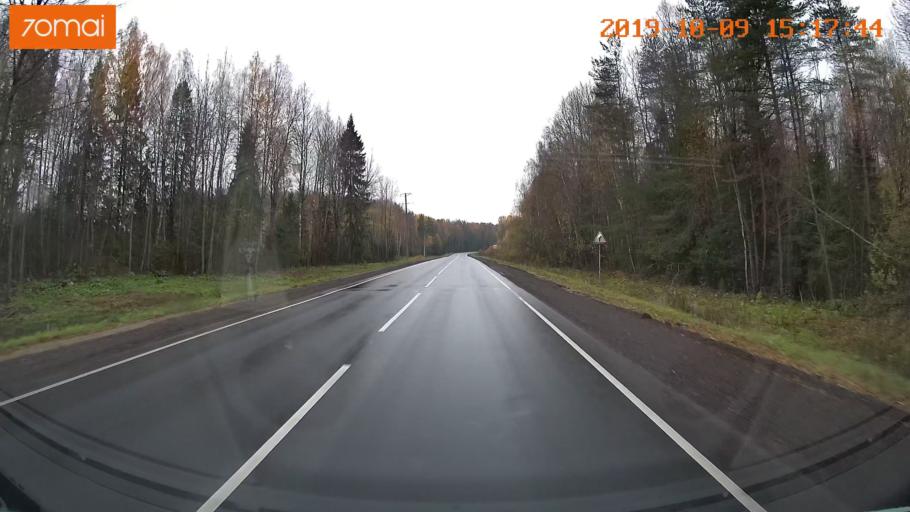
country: RU
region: Kostroma
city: Susanino
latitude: 58.0944
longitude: 41.5817
